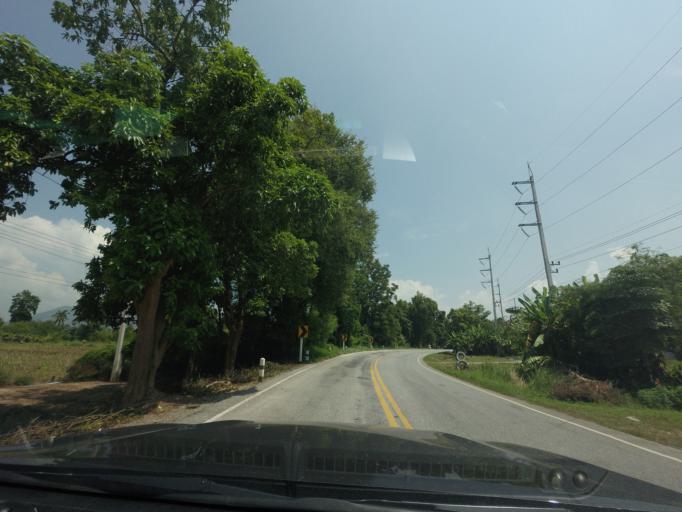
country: TH
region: Uttaradit
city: Thong Saen Khan
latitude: 17.4655
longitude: 100.2830
